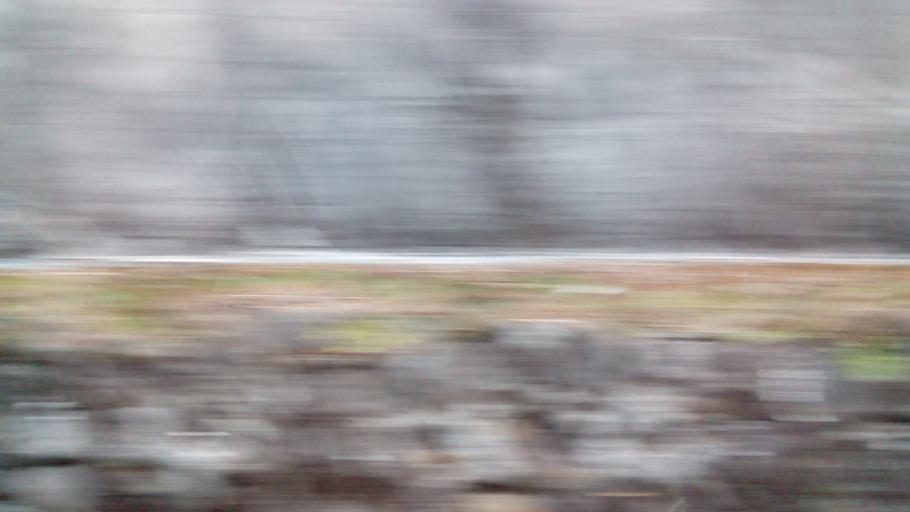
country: TW
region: Taiwan
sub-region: Hualien
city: Hualian
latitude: 24.3885
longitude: 121.3472
